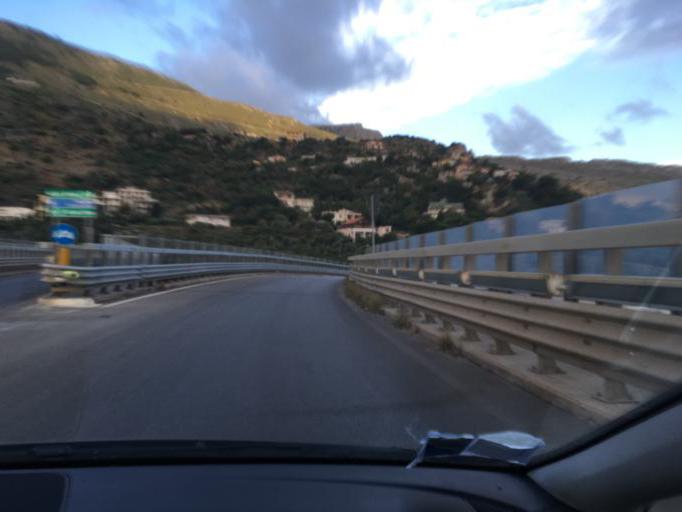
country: IT
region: Sicily
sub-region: Palermo
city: Isola delle Femmine
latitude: 38.1912
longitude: 13.2837
